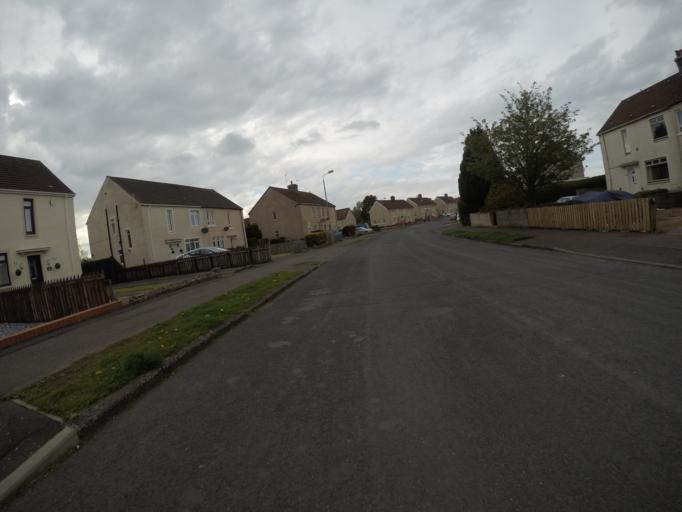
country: GB
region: Scotland
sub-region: East Ayrshire
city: Kilmaurs
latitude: 55.6404
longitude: -4.5333
